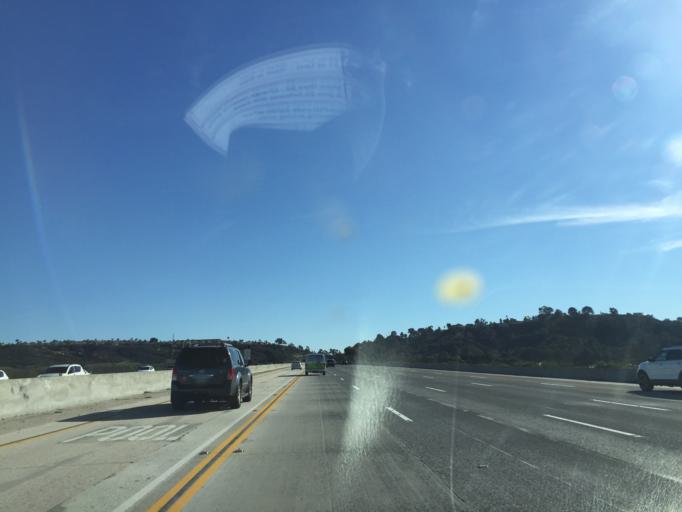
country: US
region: California
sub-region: San Diego County
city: Del Mar
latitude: 32.9699
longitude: -117.2494
